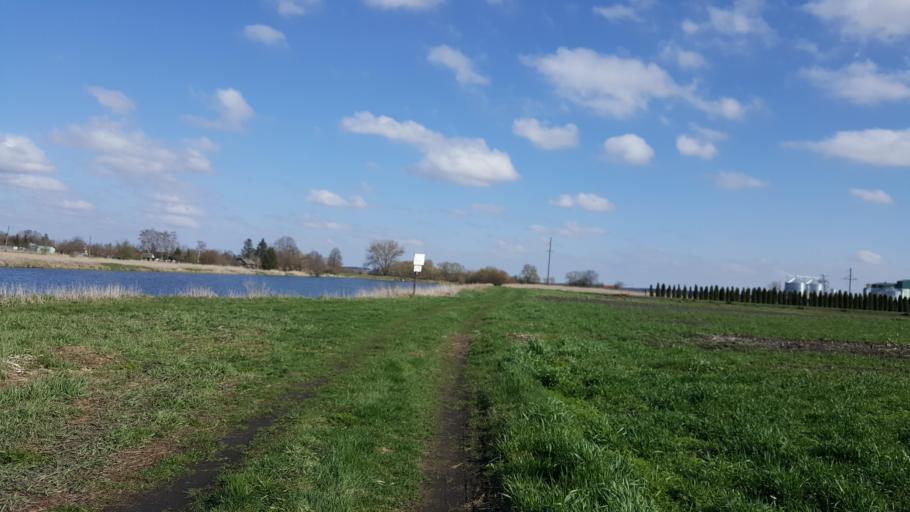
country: BY
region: Brest
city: Kamyanyets
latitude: 52.4076
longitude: 23.7753
